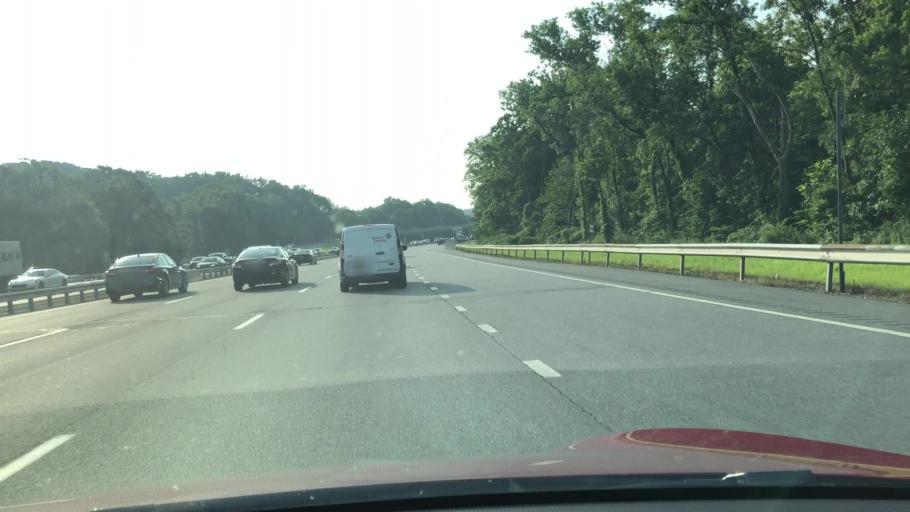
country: US
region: New York
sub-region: Westchester County
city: White Plains
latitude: 41.0292
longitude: -73.7405
